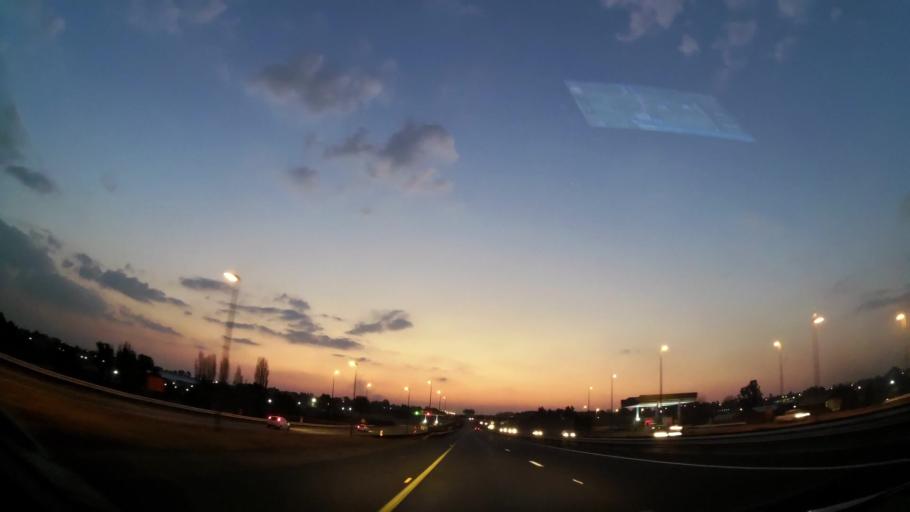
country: ZA
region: Gauteng
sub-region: Ekurhuleni Metropolitan Municipality
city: Brakpan
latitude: -26.2680
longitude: 28.3623
